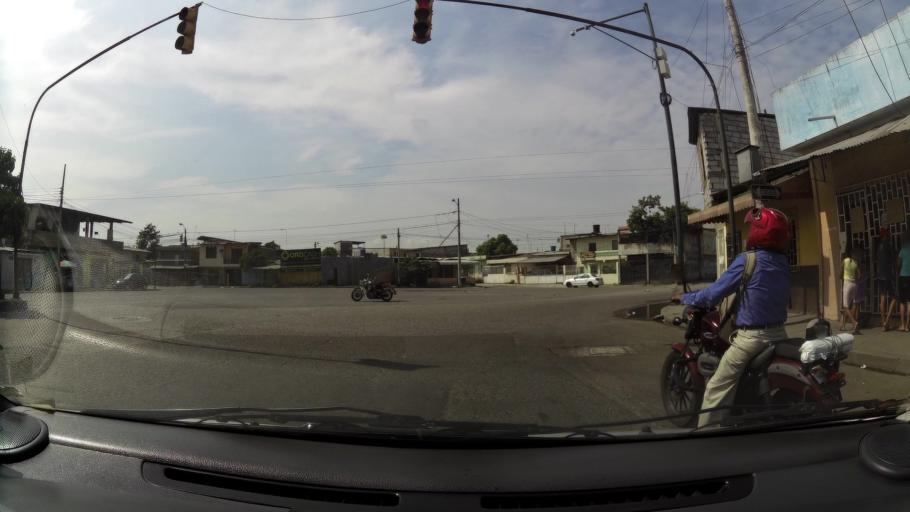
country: EC
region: Guayas
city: Guayaquil
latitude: -2.2637
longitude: -79.8890
